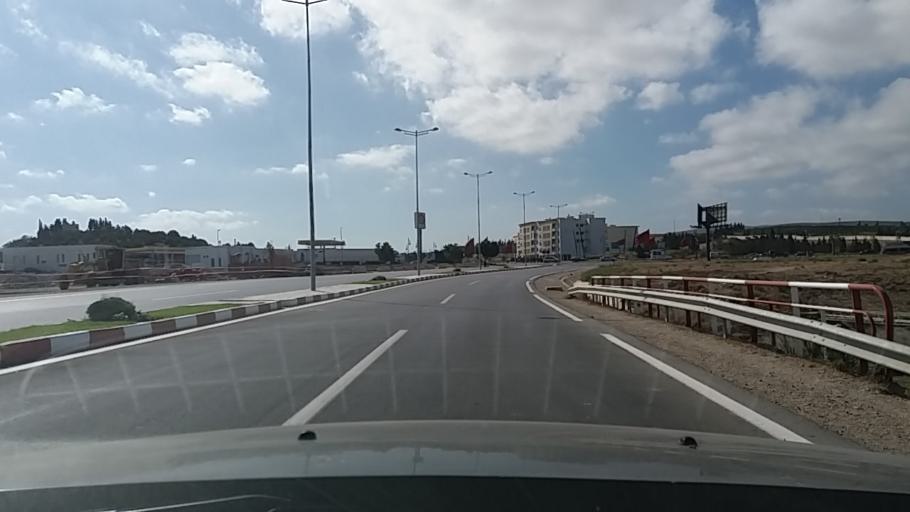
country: MA
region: Tanger-Tetouan
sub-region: Tanger-Assilah
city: Boukhalef
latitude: 35.7264
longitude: -5.8958
